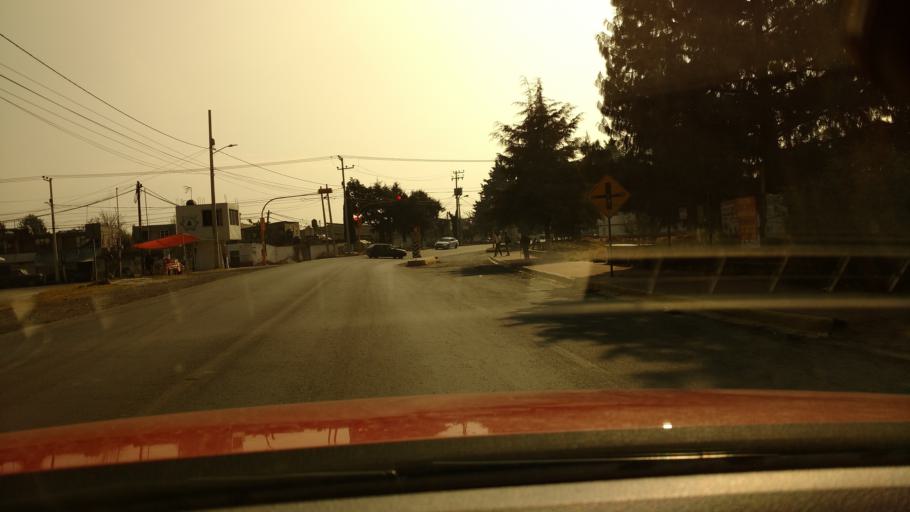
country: MX
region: Morelos
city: Chapultepec
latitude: 19.2034
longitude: -99.5519
